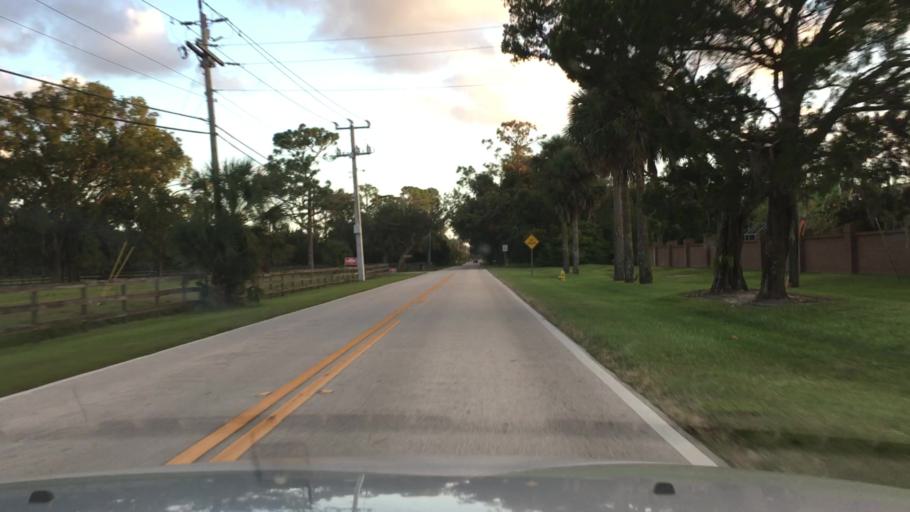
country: US
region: Florida
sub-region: Volusia County
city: Ormond Beach
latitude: 29.2869
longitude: -81.1132
